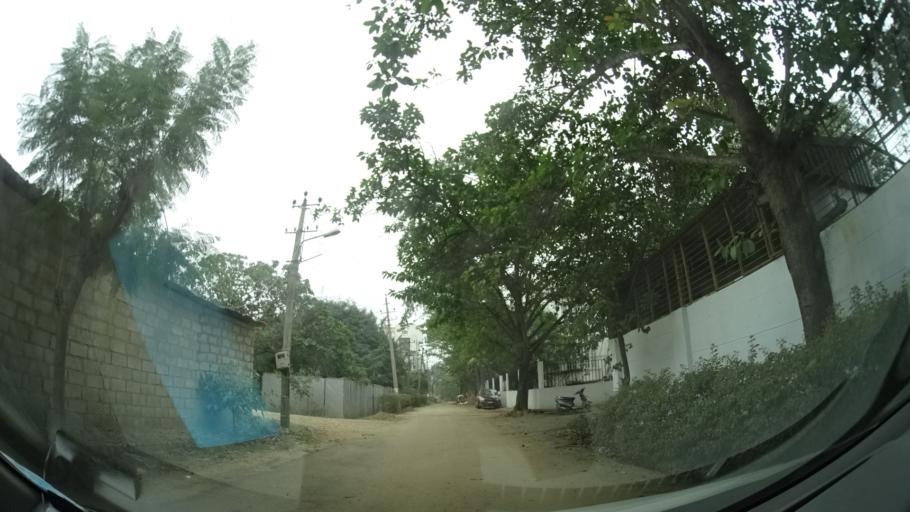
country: IN
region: Karnataka
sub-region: Bangalore Rural
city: Hoskote
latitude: 12.9711
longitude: 77.7452
